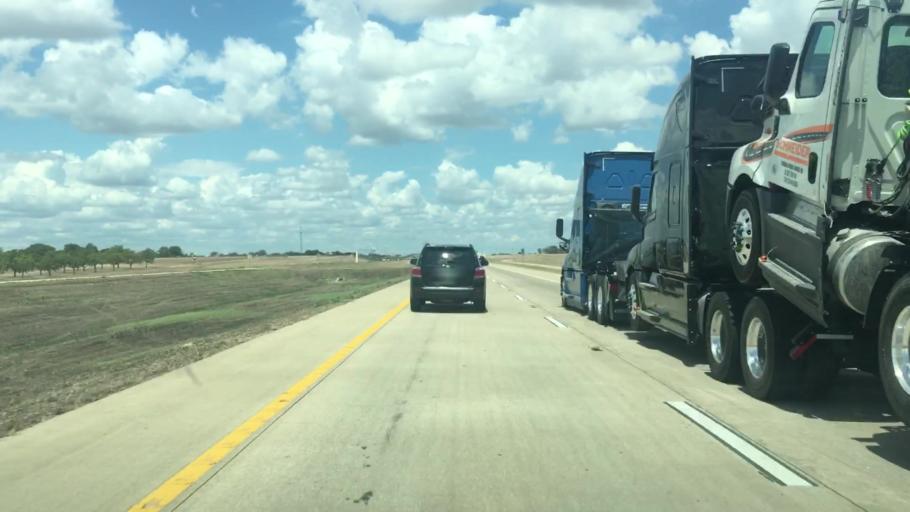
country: US
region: Texas
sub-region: Williamson County
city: Hutto
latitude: 30.5633
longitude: -97.5793
